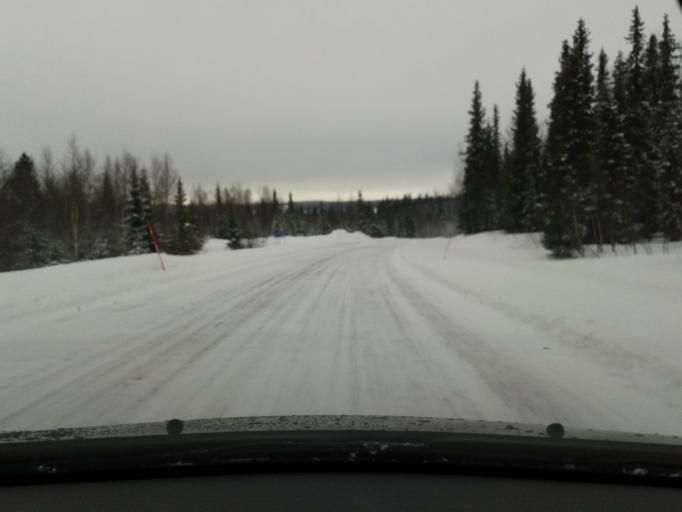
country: SE
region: Vaesterbotten
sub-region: Vilhelmina Kommun
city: Sjoberg
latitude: 65.0369
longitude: 15.9039
